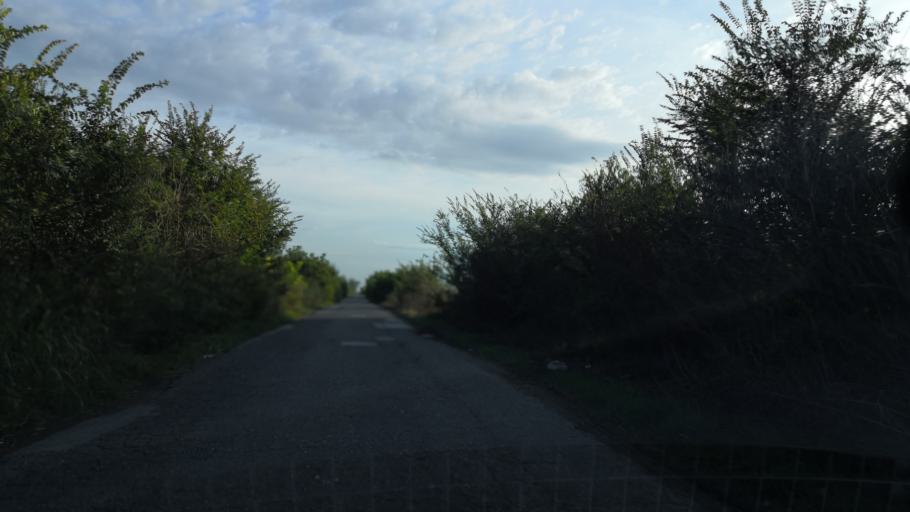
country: RS
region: Autonomna Pokrajina Vojvodina
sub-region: Sremski Okrug
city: Stara Pazova
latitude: 45.0246
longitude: 20.1707
